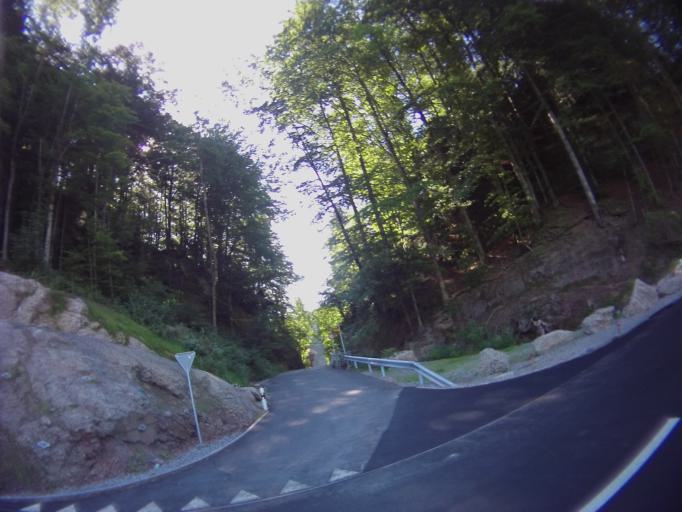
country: CH
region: Schwyz
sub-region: Bezirk Schwyz
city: Sattel
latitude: 47.0886
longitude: 8.6323
